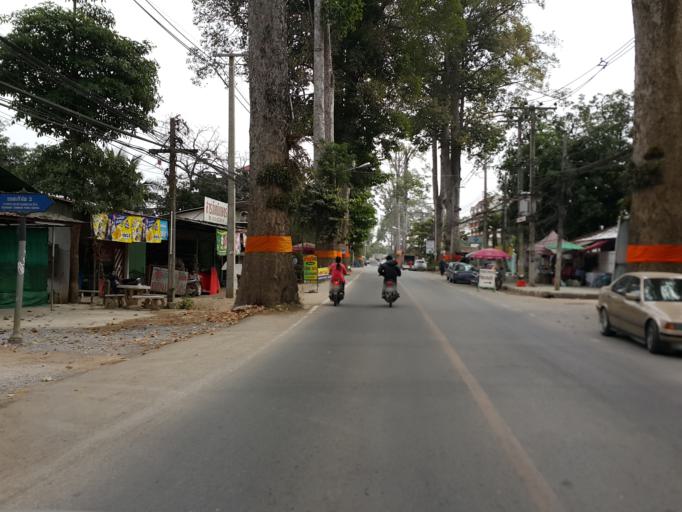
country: TH
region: Chiang Mai
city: Saraphi
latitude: 18.7167
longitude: 99.0310
